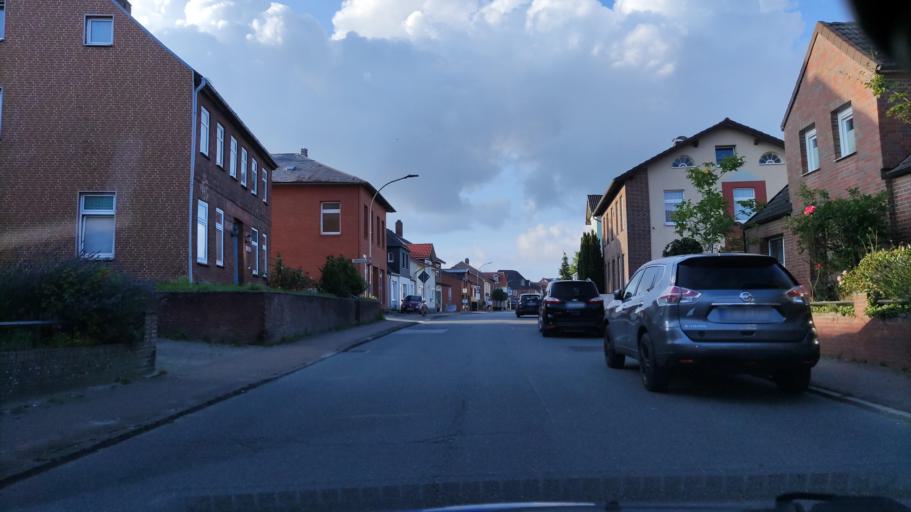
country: DE
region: Schleswig-Holstein
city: Ahrensbok
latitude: 54.0146
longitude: 10.5729
